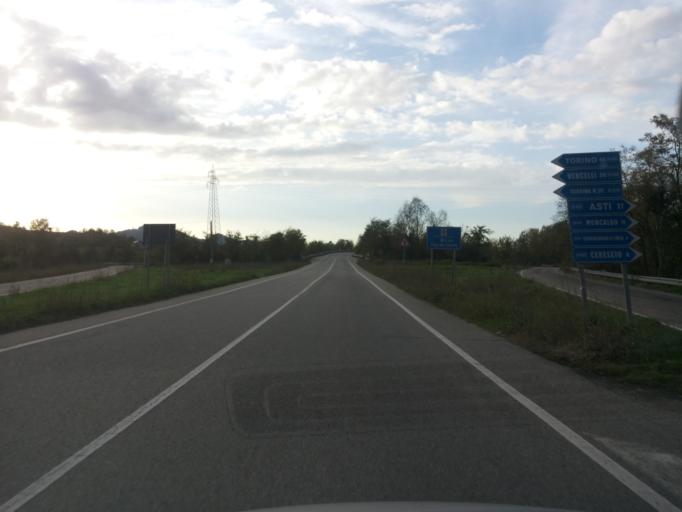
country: IT
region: Piedmont
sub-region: Provincia di Alessandria
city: Treville
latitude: 45.1080
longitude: 8.3389
